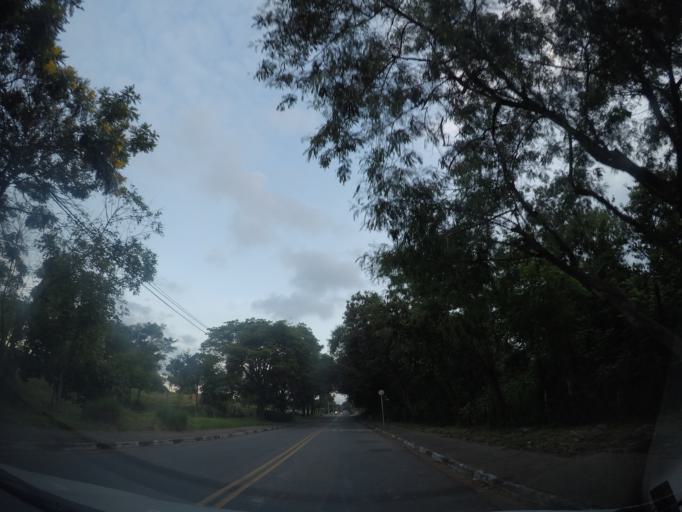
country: BR
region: Sao Paulo
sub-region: Guarulhos
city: Guarulhos
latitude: -23.4547
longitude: -46.4974
